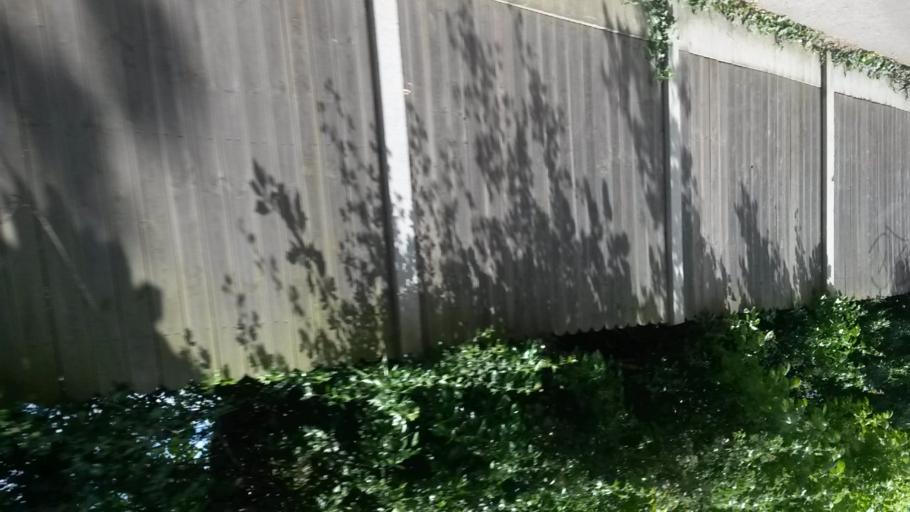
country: IE
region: Leinster
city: Donabate
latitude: 53.4899
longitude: -6.1419
